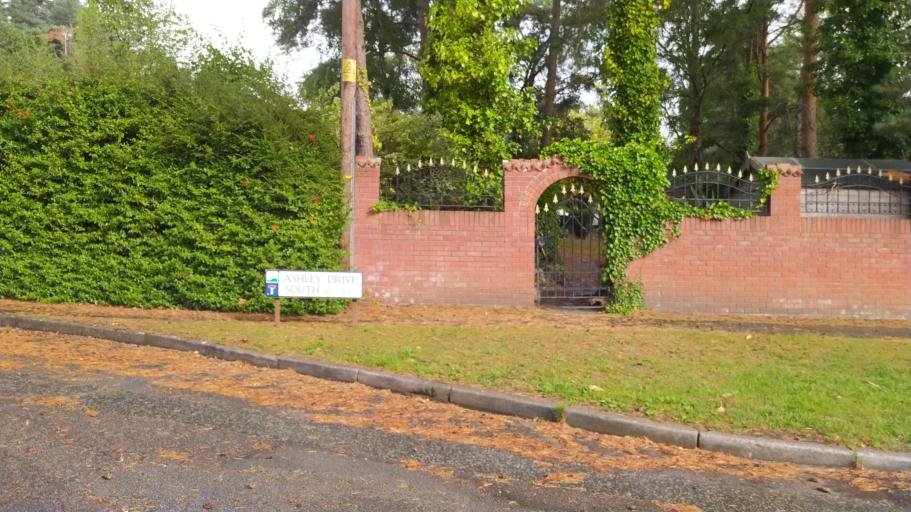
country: GB
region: England
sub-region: Dorset
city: St Leonards
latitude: 50.8367
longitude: -1.8343
